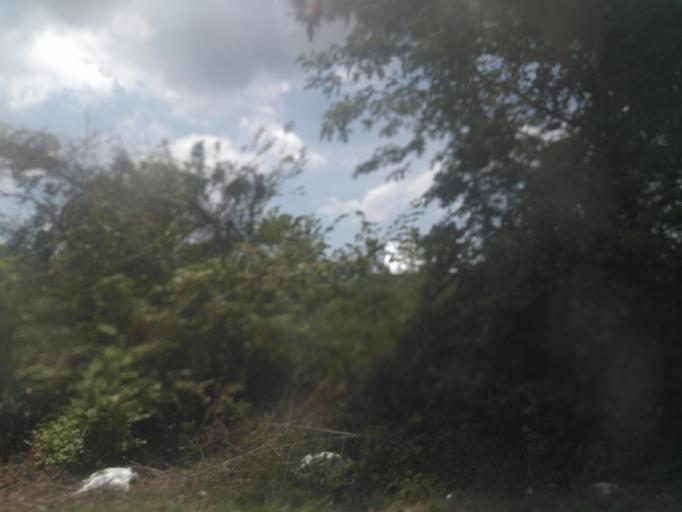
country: TZ
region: Zanzibar Urban/West
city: Zanzibar
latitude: -6.2931
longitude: 39.2877
